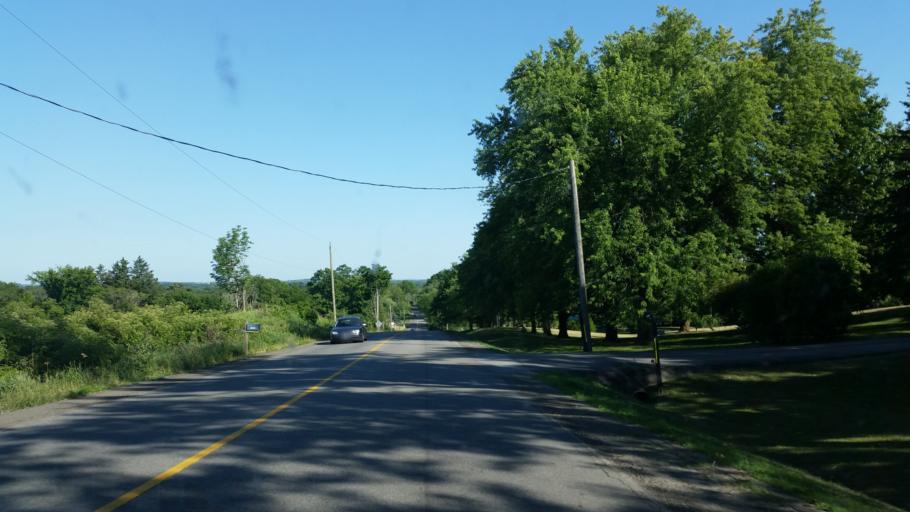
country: CA
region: Ontario
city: Bradford West Gwillimbury
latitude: 43.9561
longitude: -79.7718
